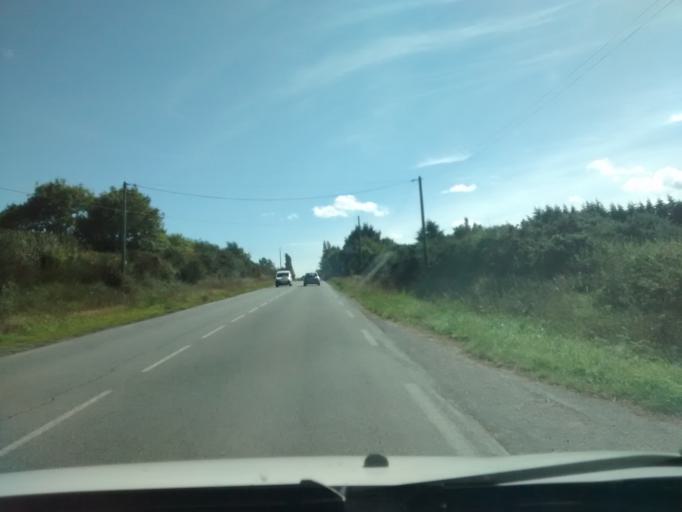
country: FR
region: Brittany
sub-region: Departement d'Ille-et-Vilaine
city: Saint-Briac-sur-Mer
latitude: 48.6164
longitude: -2.1242
